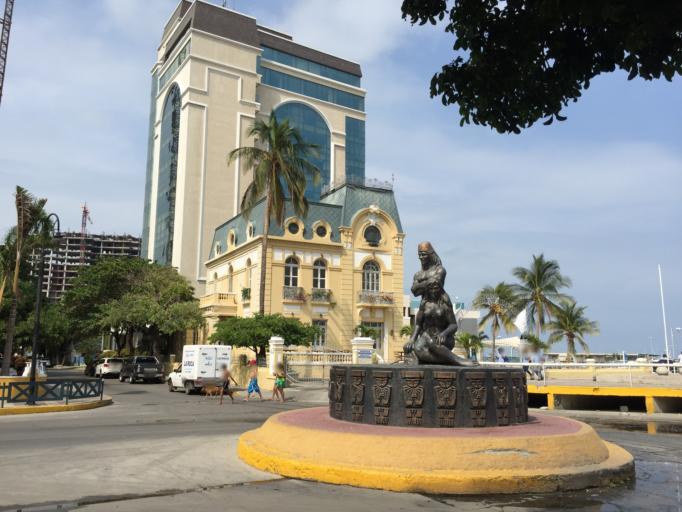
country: CO
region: Magdalena
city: Santa Marta
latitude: 11.2412
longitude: -74.2156
